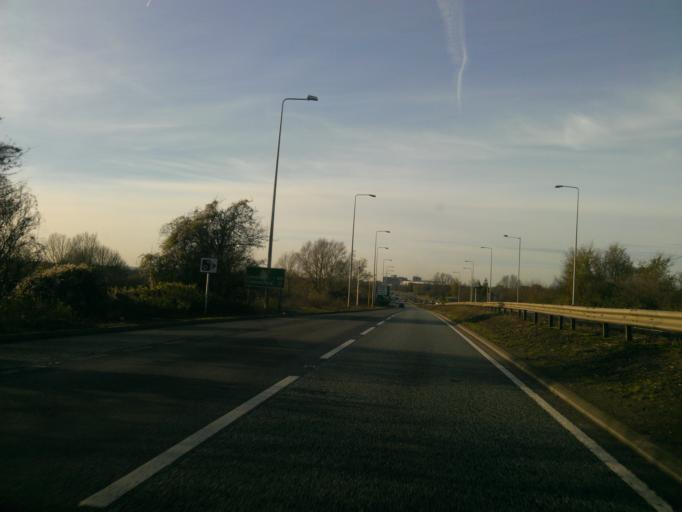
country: GB
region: England
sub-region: Essex
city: Witham
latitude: 51.8164
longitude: 0.6657
